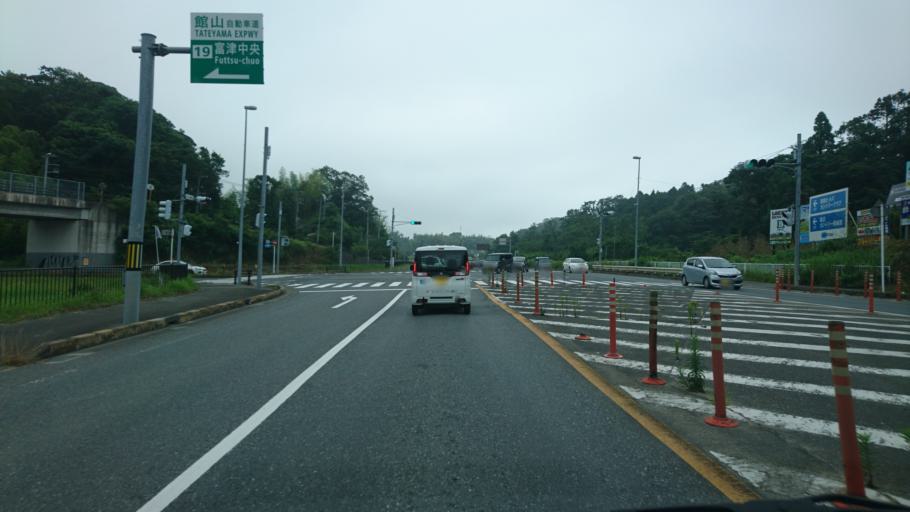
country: JP
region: Chiba
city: Kimitsu
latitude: 35.2512
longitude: 139.8857
